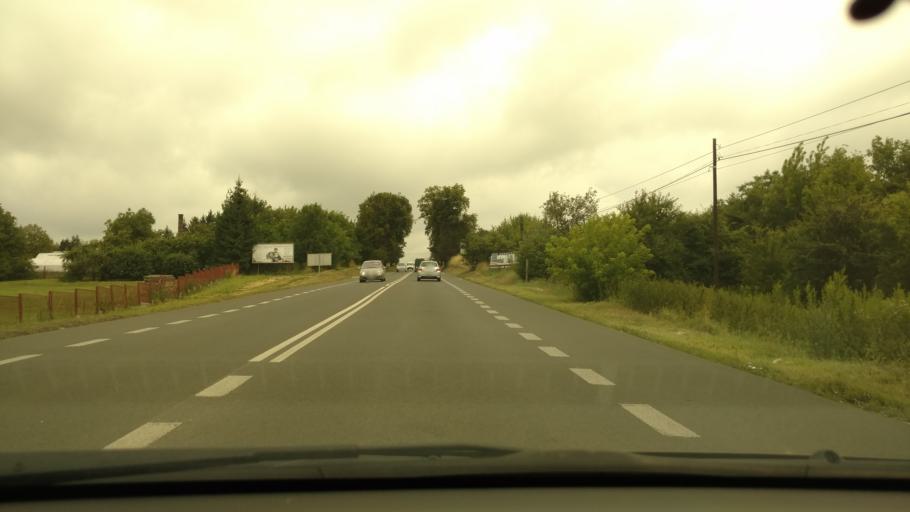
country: PL
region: Lesser Poland Voivodeship
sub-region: Powiat krakowski
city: Zielonki
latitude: 50.1066
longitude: 19.9649
